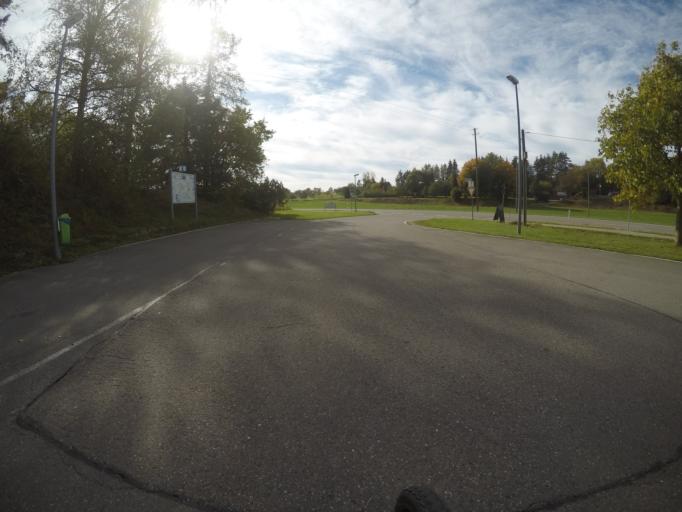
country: DE
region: Baden-Wuerttemberg
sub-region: Regierungsbezirk Stuttgart
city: Gartringen
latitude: 48.6502
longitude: 8.8873
